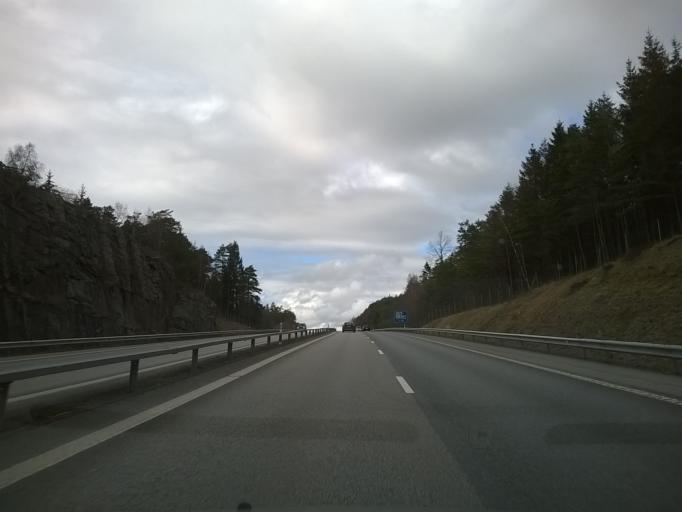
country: SE
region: Halland
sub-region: Kungsbacka Kommun
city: Frillesas
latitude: 57.3072
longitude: 12.2140
